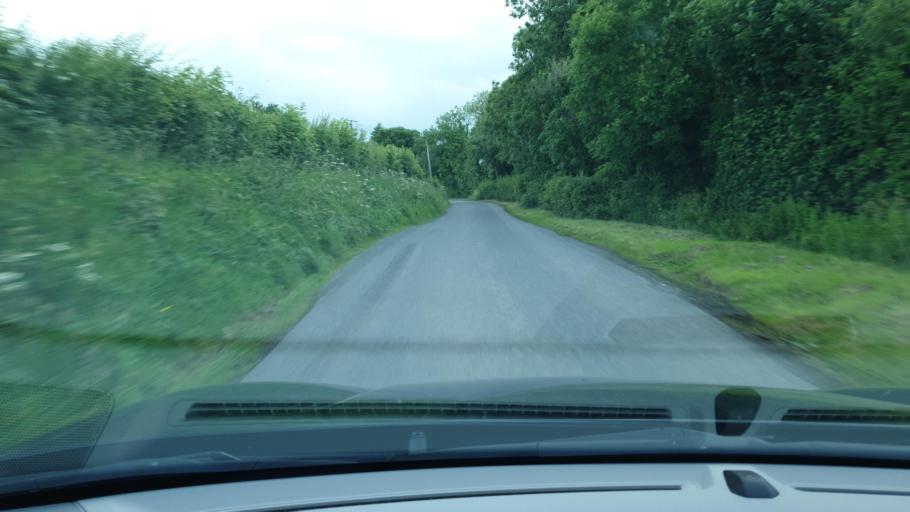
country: IE
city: Kentstown
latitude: 53.5725
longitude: -6.5007
